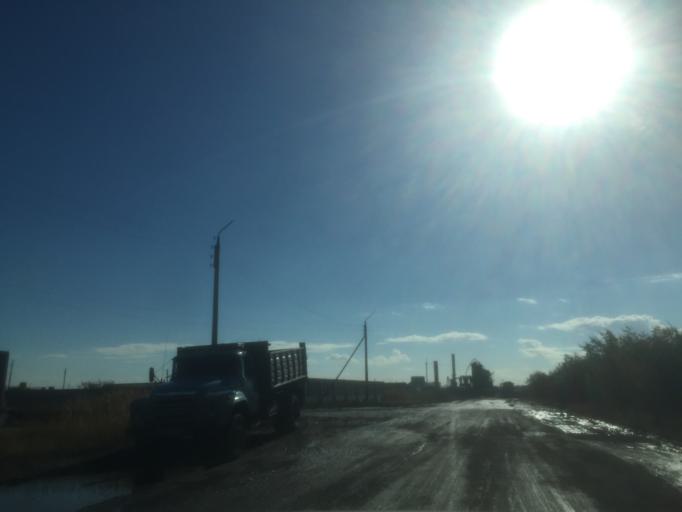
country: KZ
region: Astana Qalasy
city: Astana
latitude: 51.2152
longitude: 71.3539
